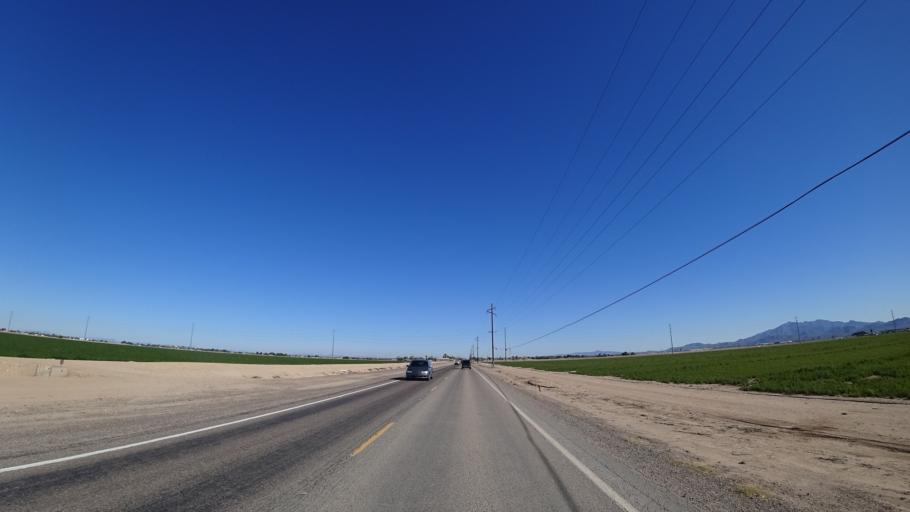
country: US
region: Arizona
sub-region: Maricopa County
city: Goodyear
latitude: 33.4356
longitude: -112.4675
